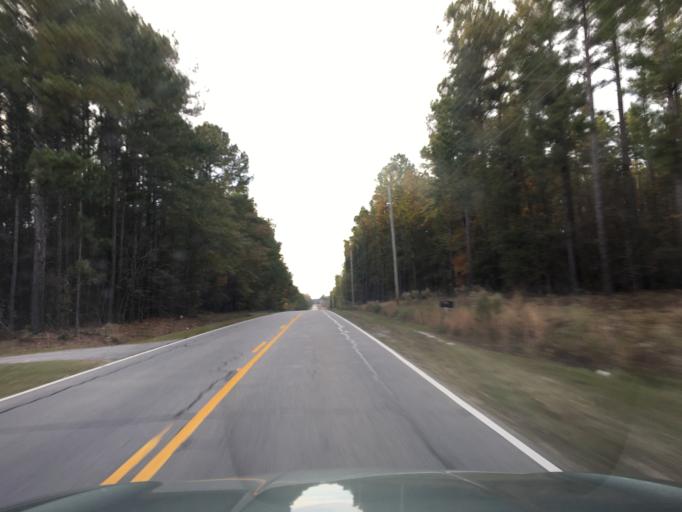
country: US
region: South Carolina
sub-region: Lexington County
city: Leesville
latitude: 33.7871
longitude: -81.4138
